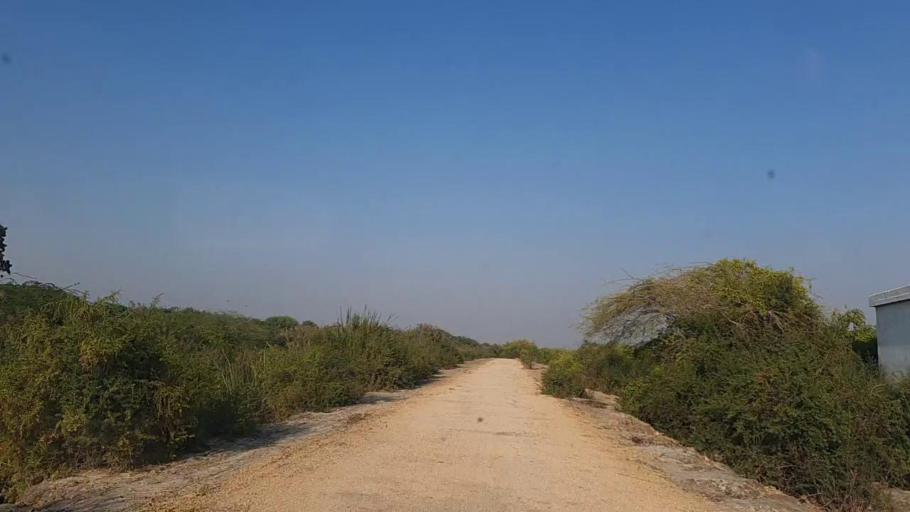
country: PK
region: Sindh
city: Thatta
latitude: 24.7264
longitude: 67.9497
